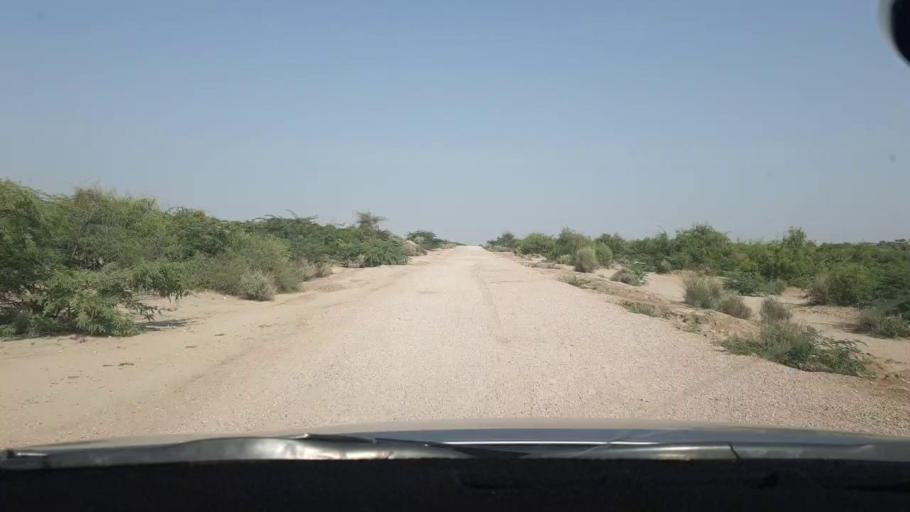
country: PK
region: Sindh
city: Pithoro
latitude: 25.7799
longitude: 69.4888
